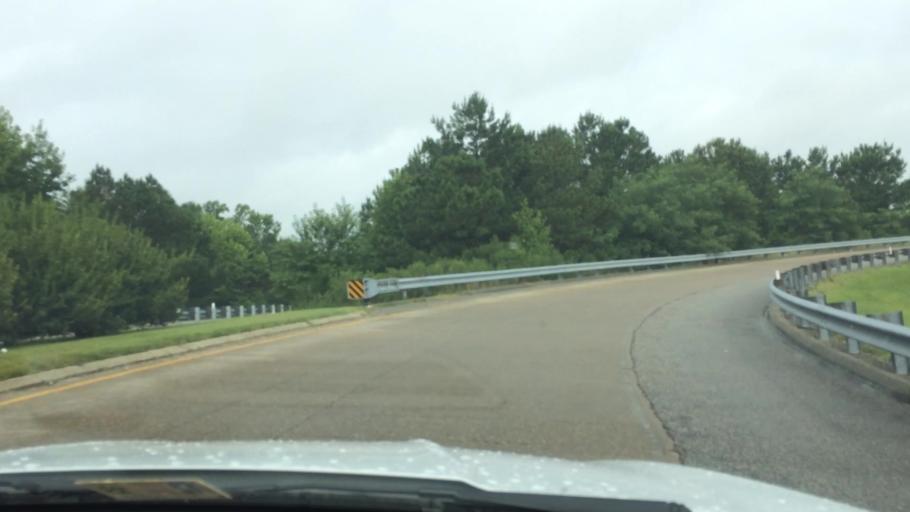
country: US
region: Virginia
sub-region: City of Williamsburg
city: Williamsburg
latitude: 37.2350
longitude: -76.6341
